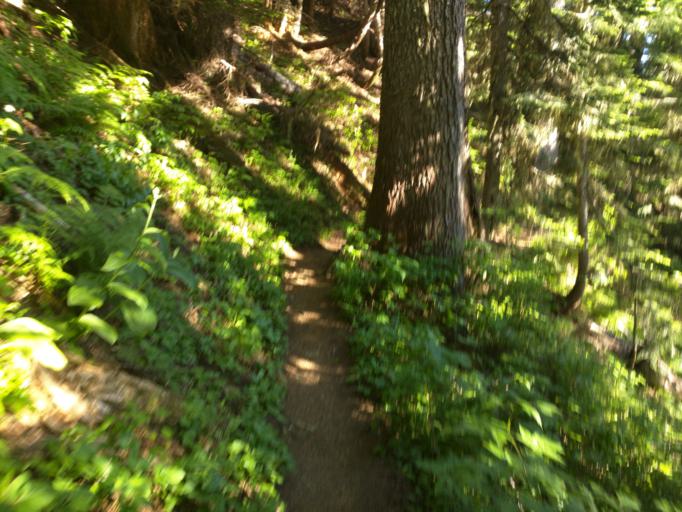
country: CA
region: British Columbia
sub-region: Fraser Valley Regional District
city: Chilliwack
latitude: 48.9246
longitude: -121.8577
